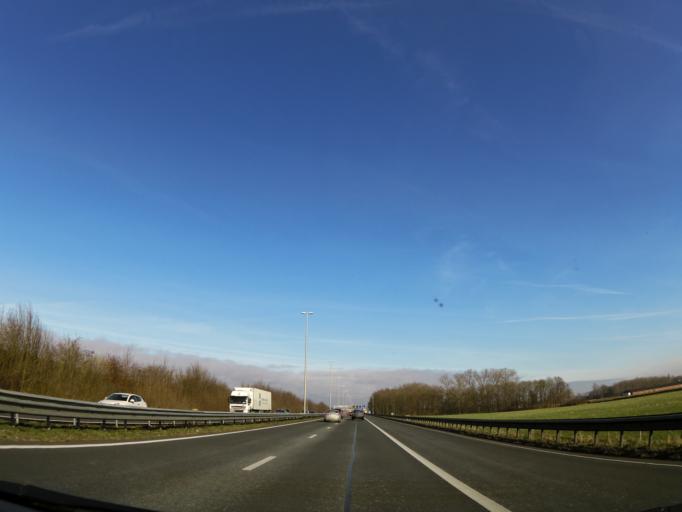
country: BE
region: Flanders
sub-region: Provincie Limburg
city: Maaseik
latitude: 51.0890
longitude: 5.8350
